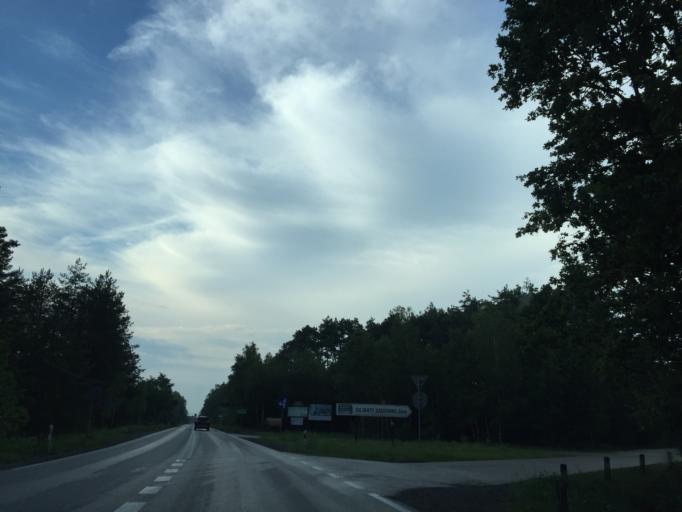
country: PL
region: Masovian Voivodeship
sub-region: Powiat wegrowski
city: Sadowne
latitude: 52.6272
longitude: 21.8441
